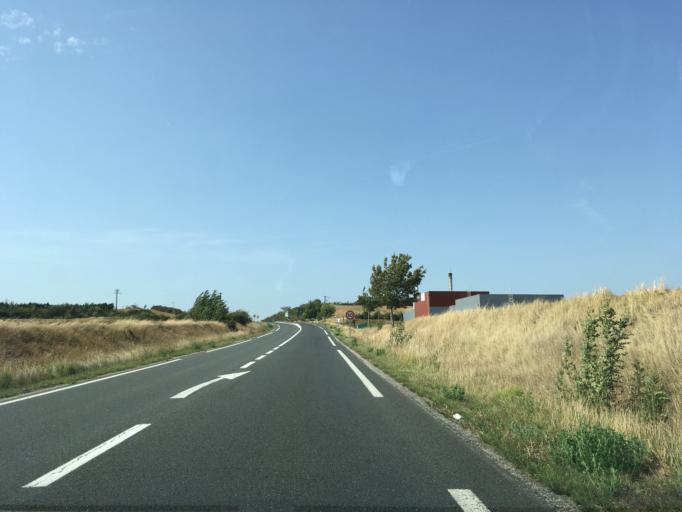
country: FR
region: Midi-Pyrenees
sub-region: Departement du Tarn
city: Lagarrigue
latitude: 43.5759
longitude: 2.2614
